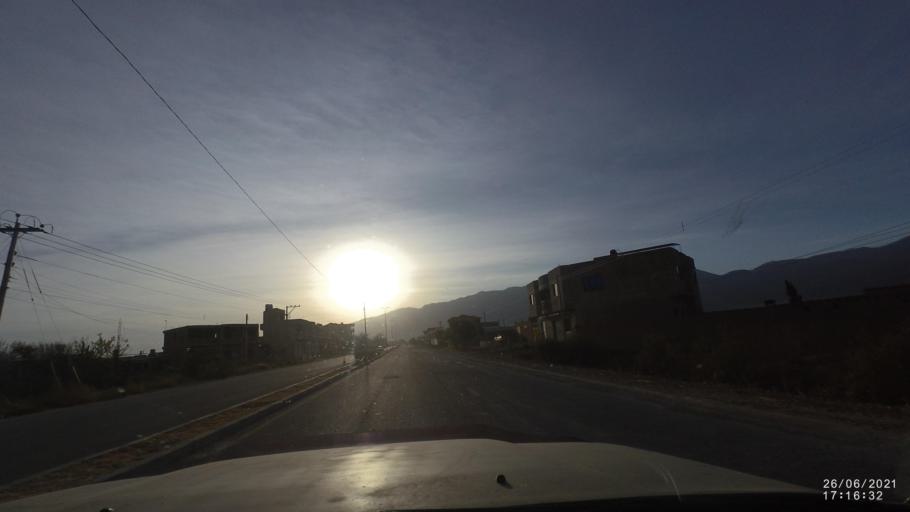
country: BO
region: Cochabamba
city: Cliza
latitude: -17.5582
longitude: -65.9391
